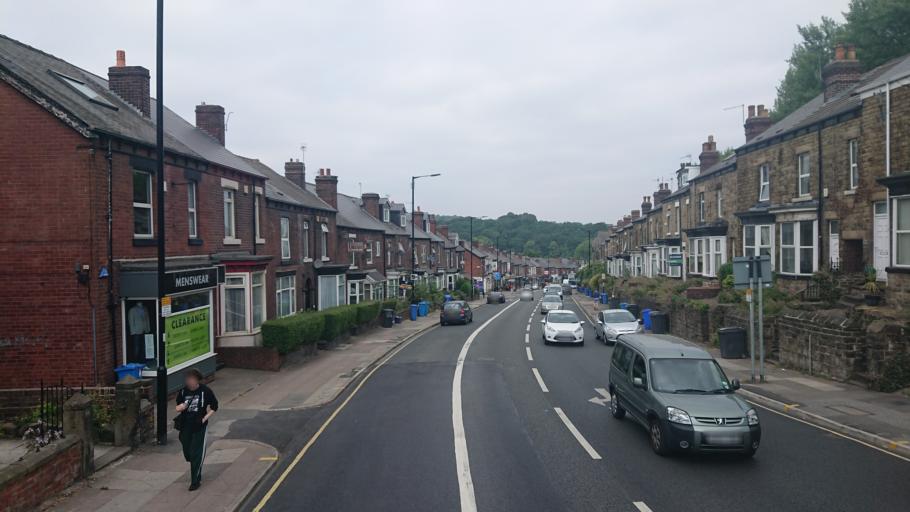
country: GB
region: England
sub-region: Sheffield
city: Sheffield
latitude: 53.3646
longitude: -1.5080
